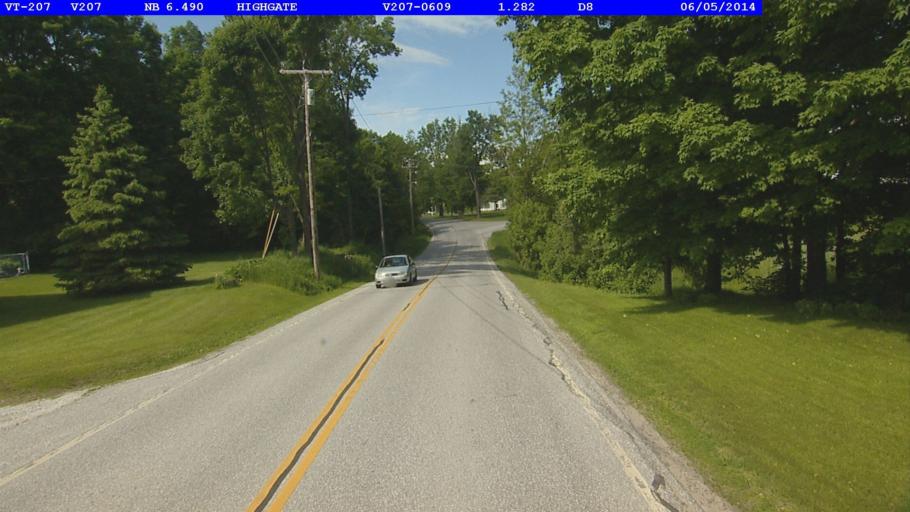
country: US
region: Vermont
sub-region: Franklin County
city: Swanton
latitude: 44.9290
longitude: -73.0496
